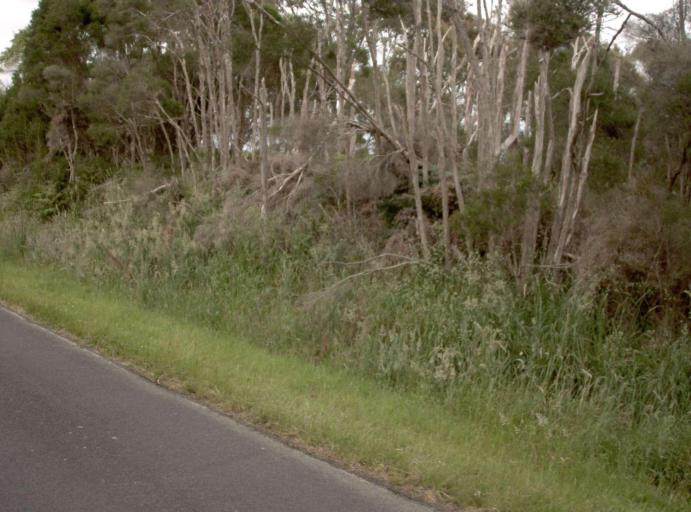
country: AU
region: Victoria
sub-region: Bass Coast
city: North Wonthaggi
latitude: -38.5396
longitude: 145.6981
